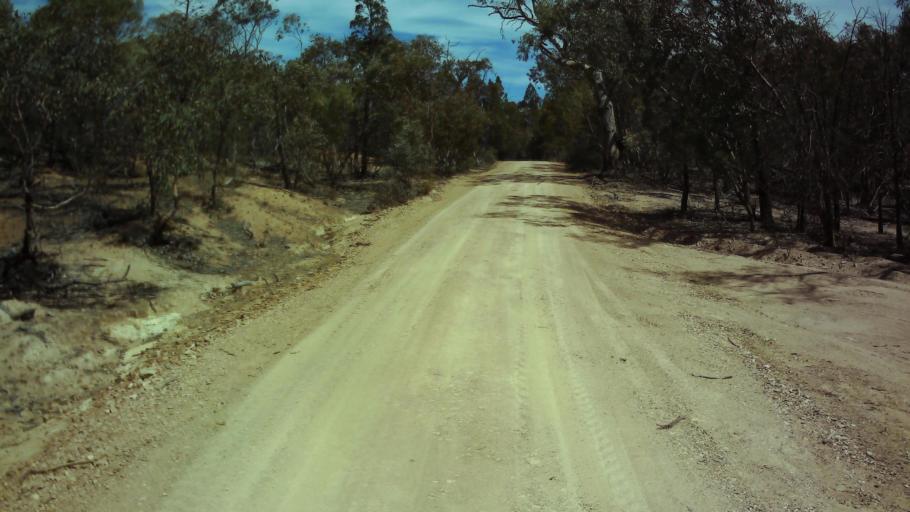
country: AU
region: New South Wales
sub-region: Weddin
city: Grenfell
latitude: -33.8051
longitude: 148.1606
